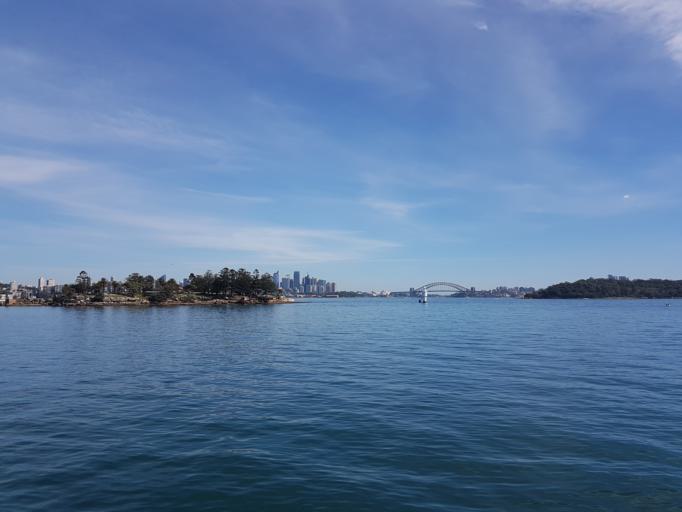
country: AU
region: New South Wales
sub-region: Woollahra
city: Point Piper
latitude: -33.8569
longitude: 151.2621
